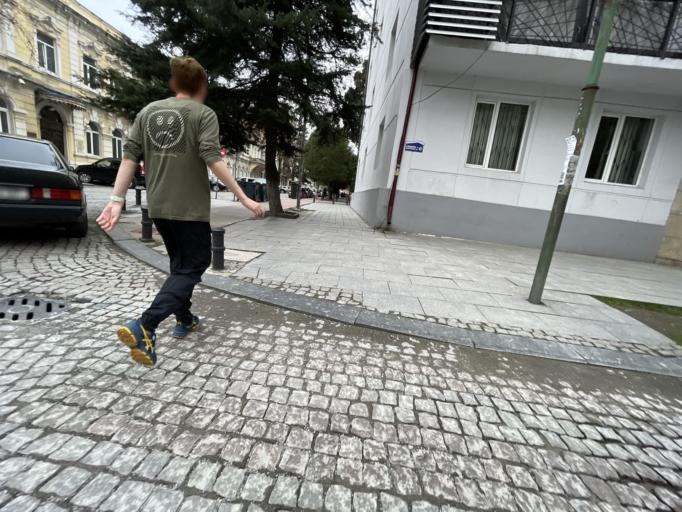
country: GE
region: Ajaria
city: Batumi
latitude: 41.6502
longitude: 41.6300
